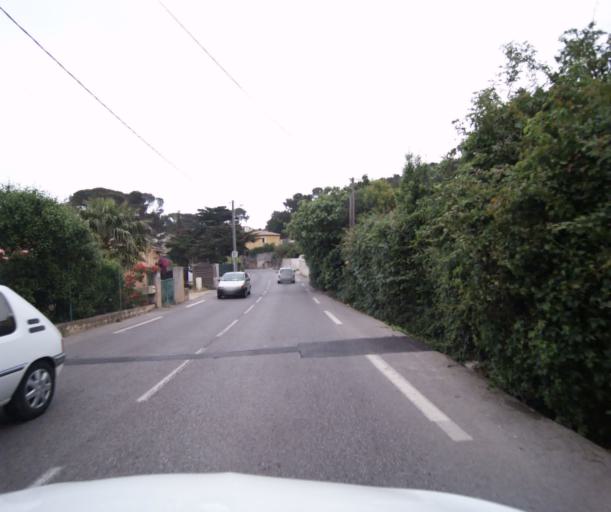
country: FR
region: Provence-Alpes-Cote d'Azur
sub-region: Departement du Var
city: La Seyne-sur-Mer
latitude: 43.0897
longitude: 5.8719
